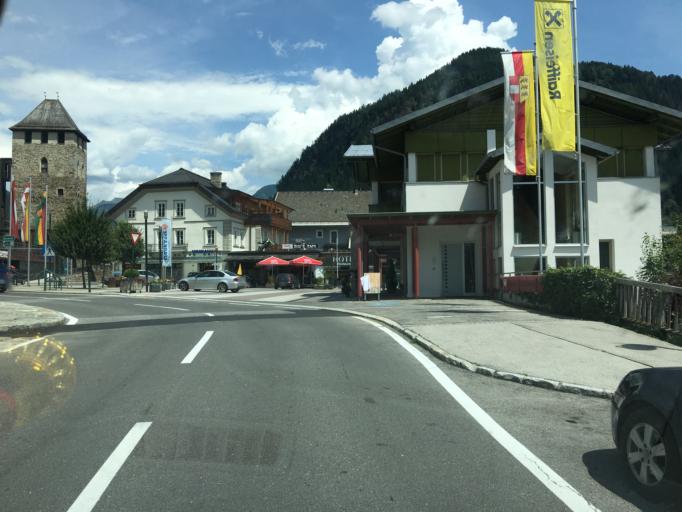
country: AT
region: Carinthia
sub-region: Politischer Bezirk Spittal an der Drau
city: Winklern
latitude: 46.8702
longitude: 12.8768
